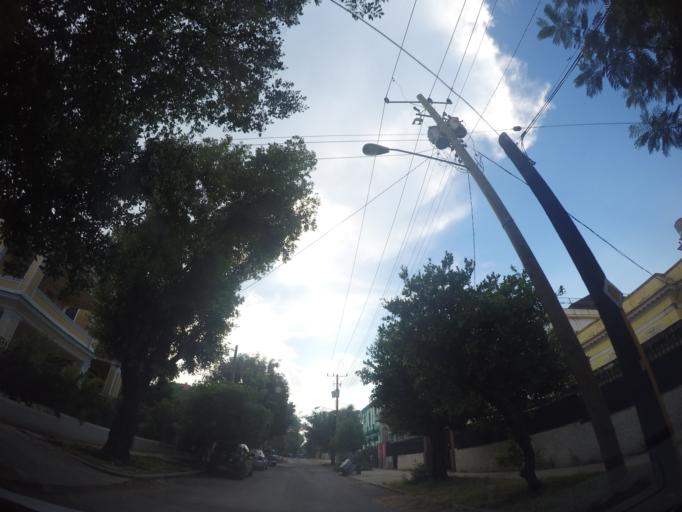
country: CU
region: La Habana
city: Havana
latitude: 23.1377
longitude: -82.3900
